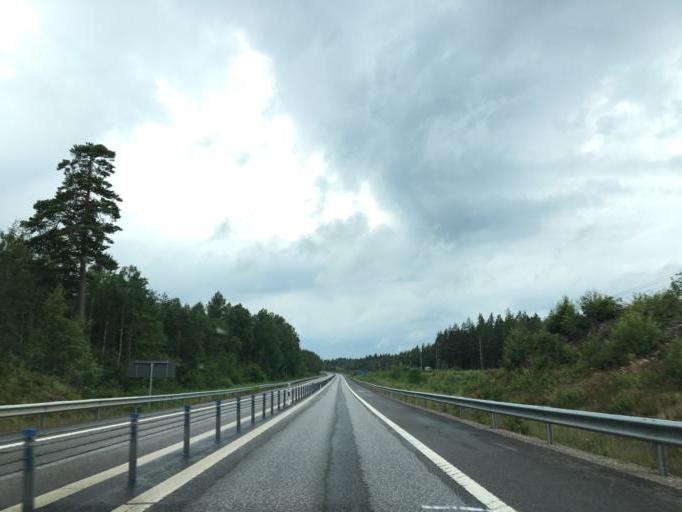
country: SE
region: OEstergoetland
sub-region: Norrkopings Kommun
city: Jursla
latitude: 58.8243
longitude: 16.1761
